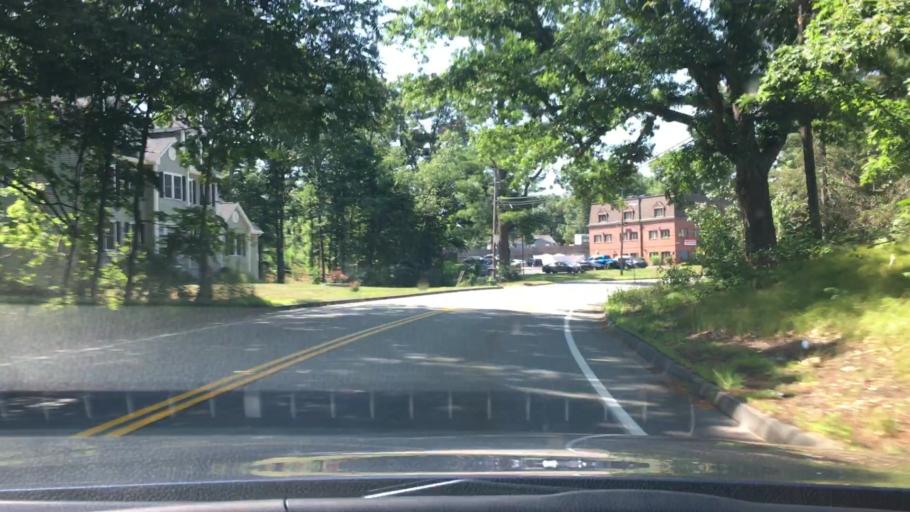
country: US
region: Massachusetts
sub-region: Middlesex County
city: Billerica
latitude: 42.5744
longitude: -71.2895
